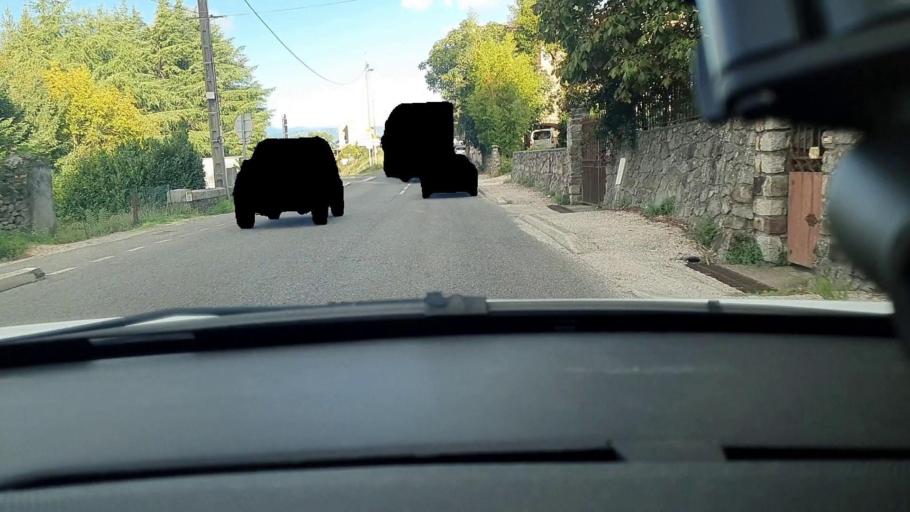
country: FR
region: Languedoc-Roussillon
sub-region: Departement du Gard
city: Molieres-sur-Ceze
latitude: 44.2783
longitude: 4.1305
